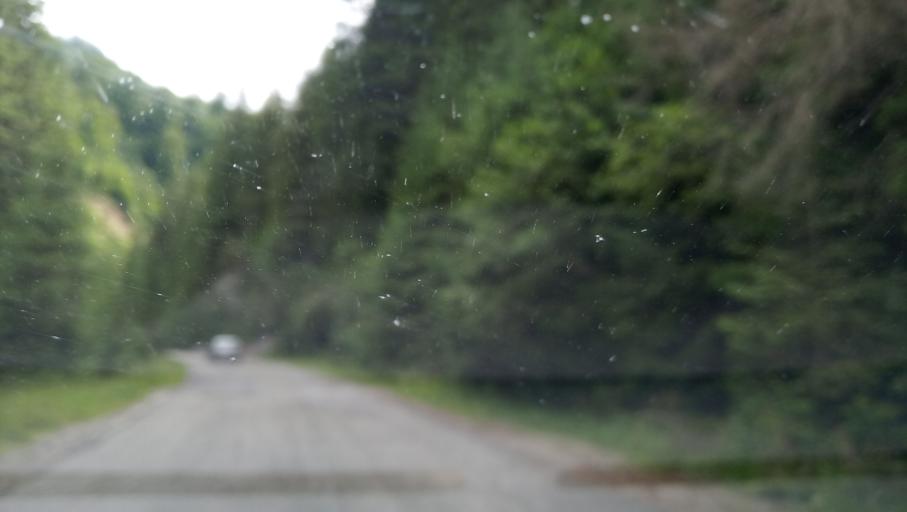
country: RO
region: Hunedoara
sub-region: Oras Petrila
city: Petrila
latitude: 45.4096
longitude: 23.5408
